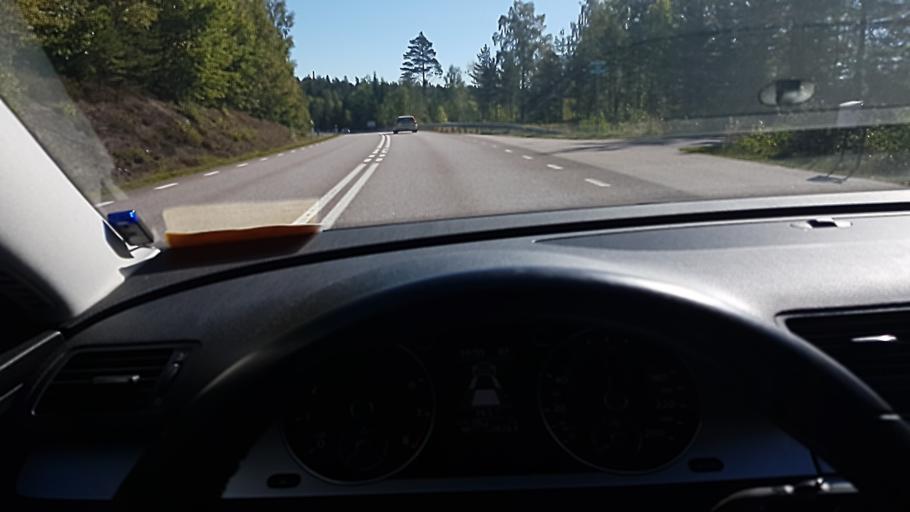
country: SE
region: Kronoberg
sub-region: Lessebo Kommun
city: Lessebo
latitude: 56.7810
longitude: 15.2044
